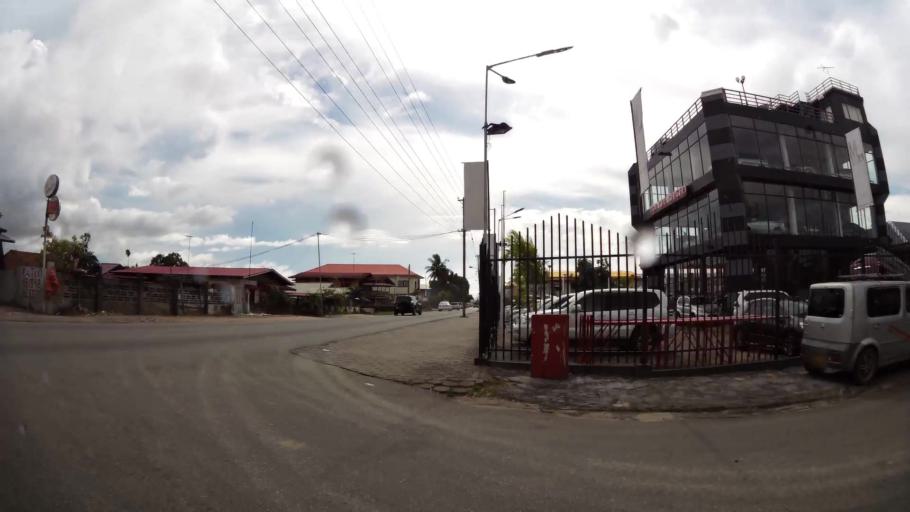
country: SR
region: Paramaribo
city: Paramaribo
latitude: 5.8419
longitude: -55.1930
